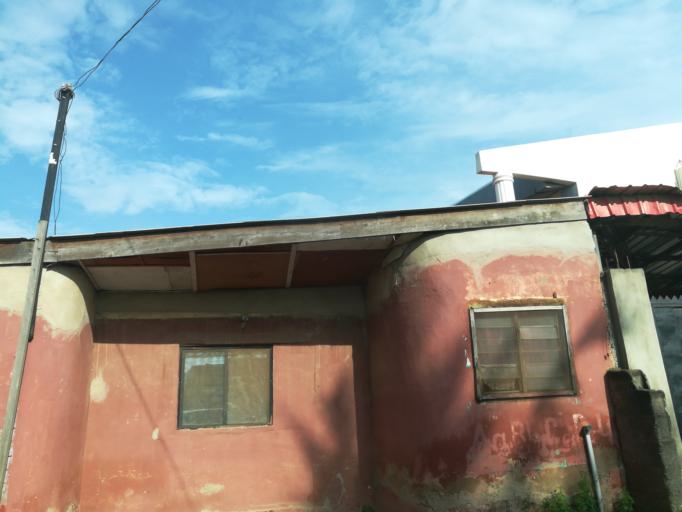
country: NG
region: Lagos
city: Ojota
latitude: 6.6028
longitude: 3.4218
